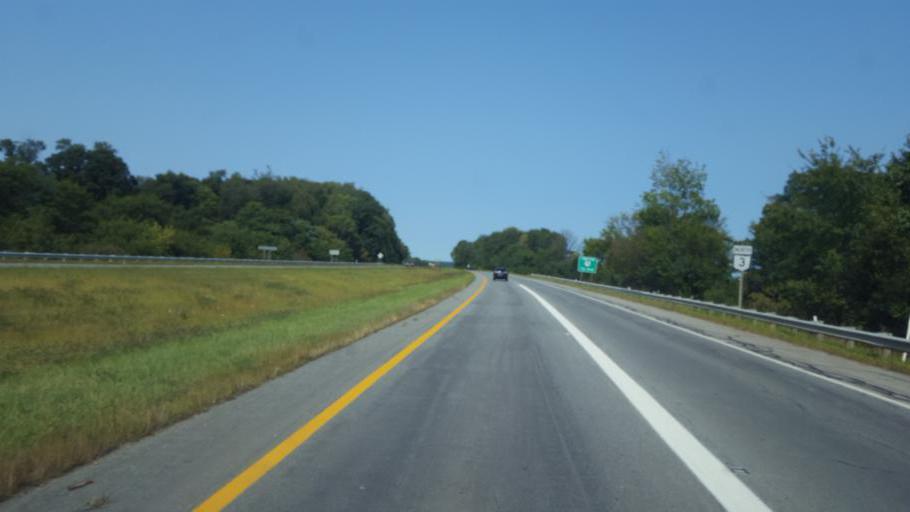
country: US
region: Ohio
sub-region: Wayne County
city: Wooster
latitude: 40.7722
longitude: -81.9725
